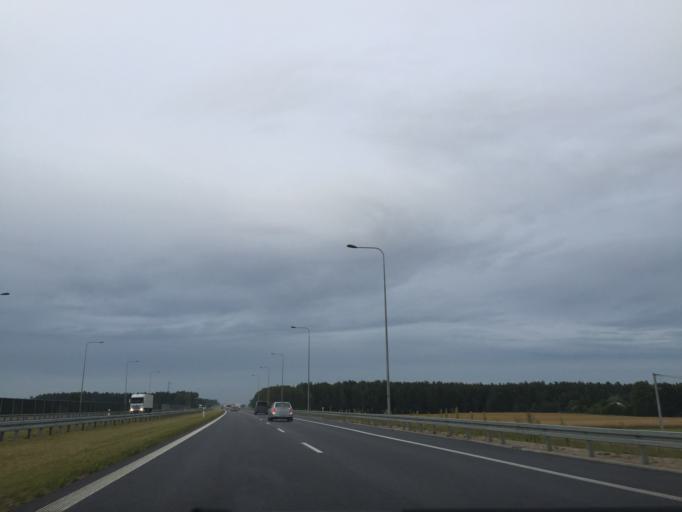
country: PL
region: Podlasie
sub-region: Powiat zambrowski
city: Rutki-Kossaki
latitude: 53.0616
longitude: 22.4047
